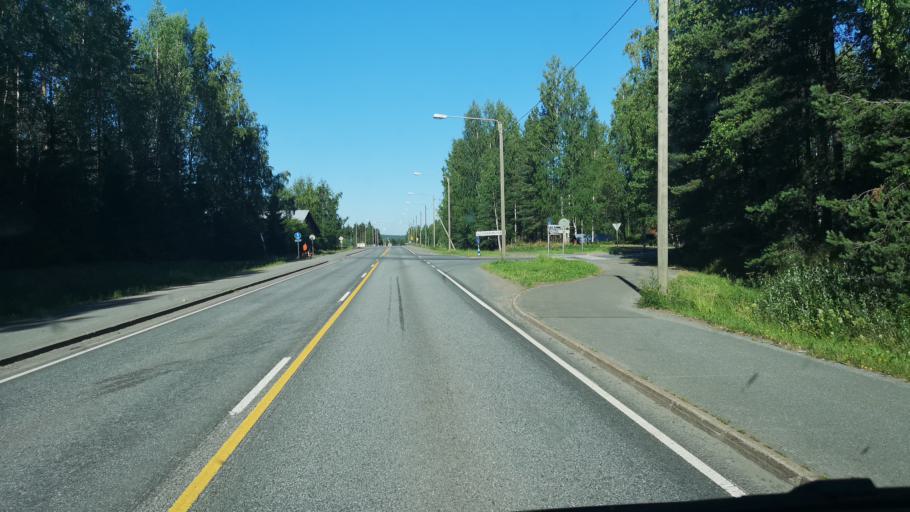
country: FI
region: Southern Ostrobothnia
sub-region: Seinaejoki
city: Lapua
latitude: 62.9693
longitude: 23.0553
